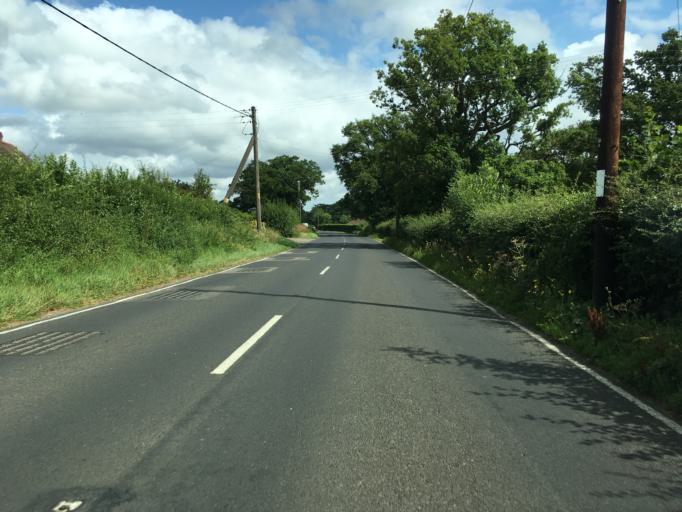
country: GB
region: England
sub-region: Kent
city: Tenterden
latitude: 51.1031
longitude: 0.6560
